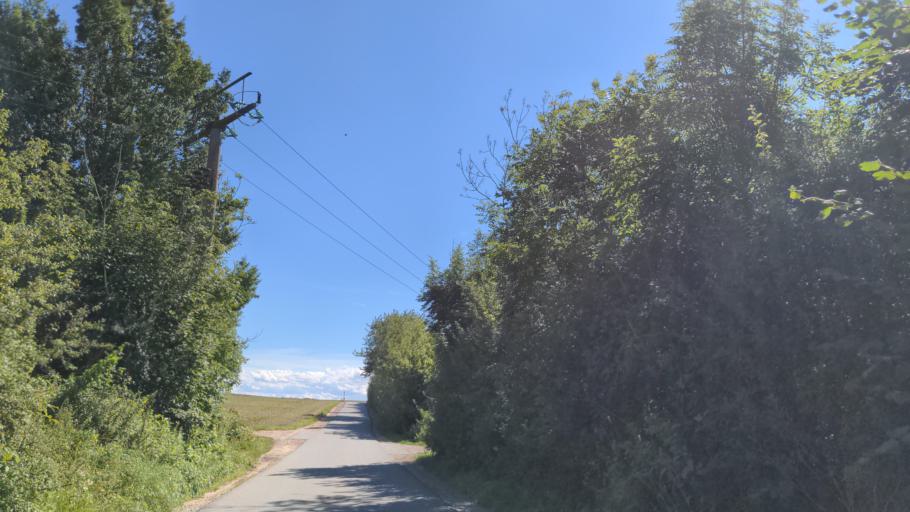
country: DE
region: Schleswig-Holstein
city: Altenkrempe
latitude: 54.1696
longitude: 10.7995
